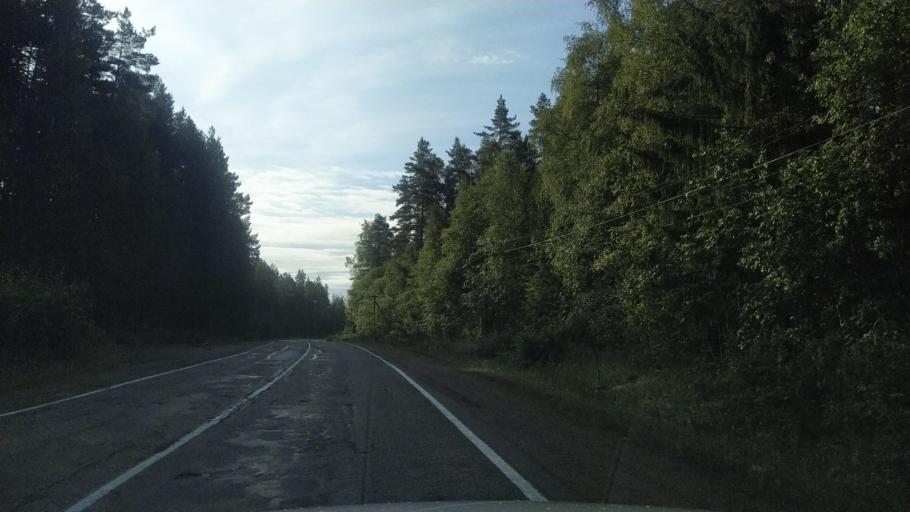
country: RU
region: Leningrad
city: Priozersk
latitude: 60.9891
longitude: 30.2595
